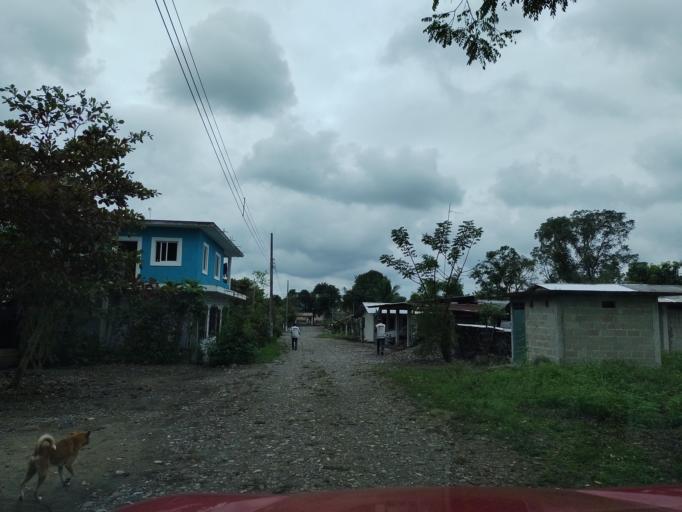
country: MX
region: Veracruz
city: Agua Dulce
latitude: 20.3031
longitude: -97.3432
